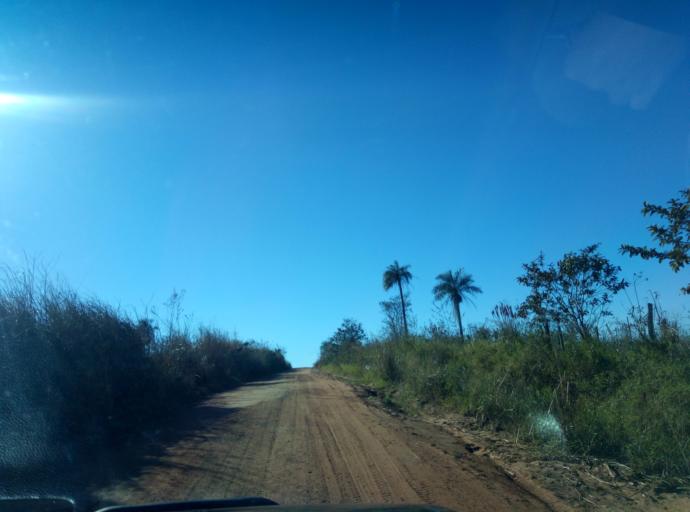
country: PY
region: Caaguazu
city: Doctor Cecilio Baez
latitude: -25.1593
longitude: -56.2878
